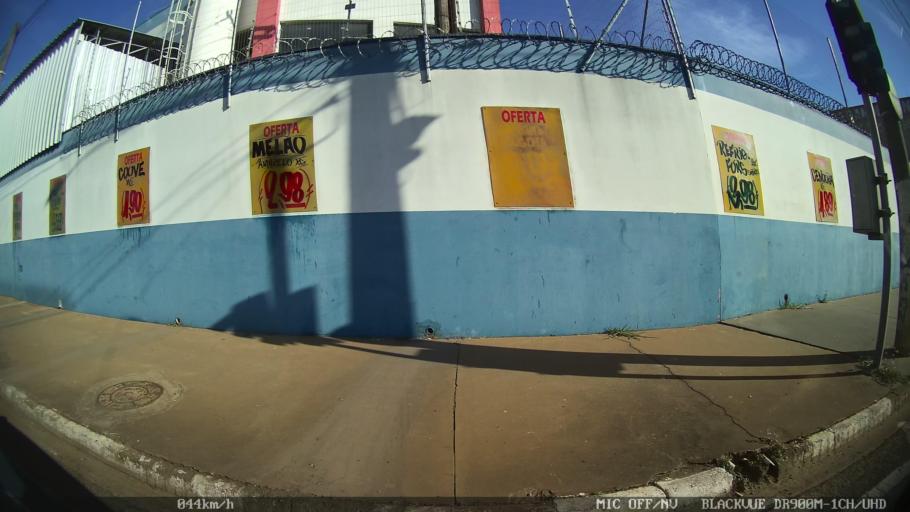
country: BR
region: Sao Paulo
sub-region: Franca
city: Franca
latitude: -20.5069
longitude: -47.3955
